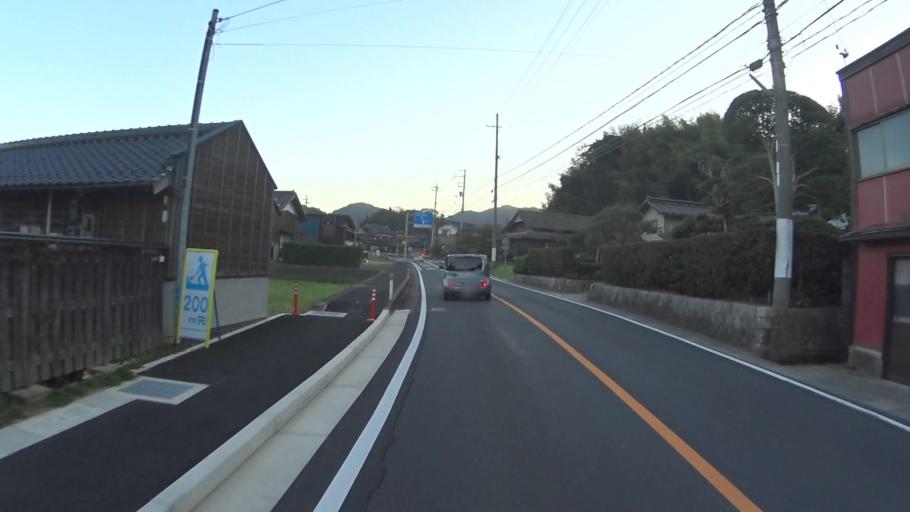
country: JP
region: Kyoto
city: Miyazu
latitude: 35.6538
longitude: 135.0321
